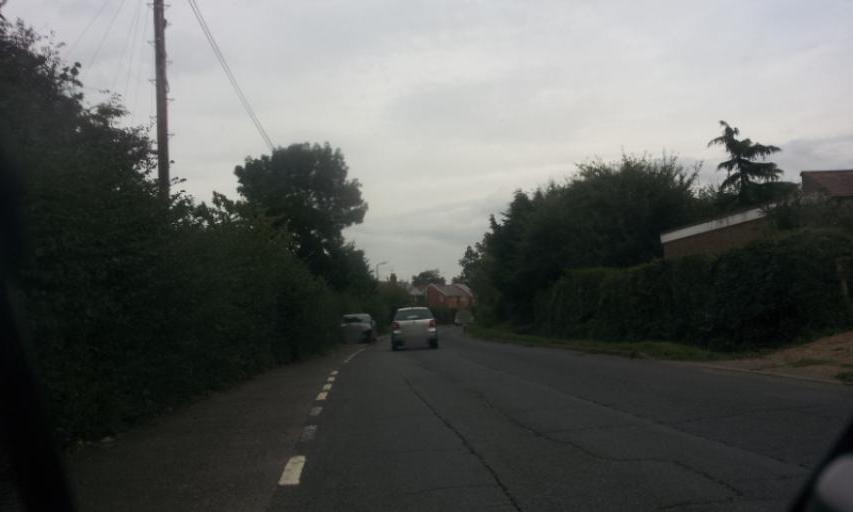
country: GB
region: England
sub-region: Kent
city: Hadlow
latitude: 51.2100
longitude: 0.3463
